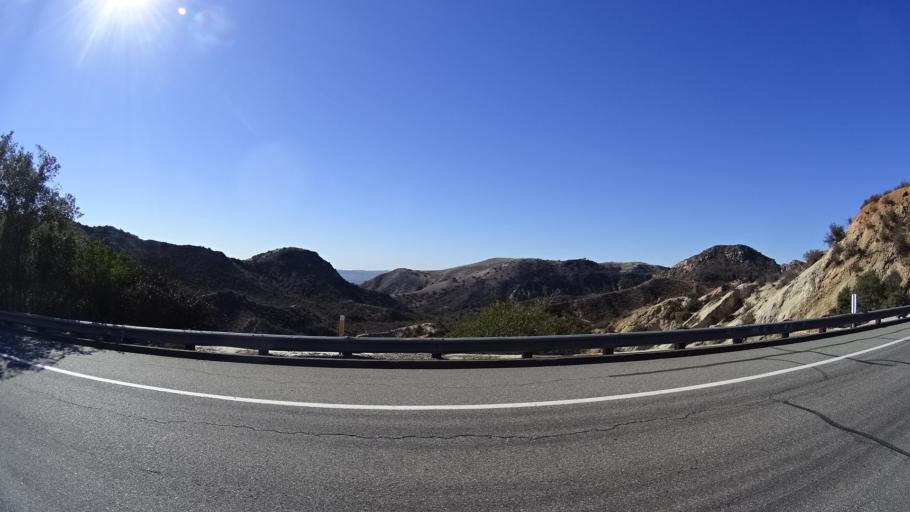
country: US
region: California
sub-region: Orange County
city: Foothill Ranch
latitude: 33.7023
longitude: -117.6417
